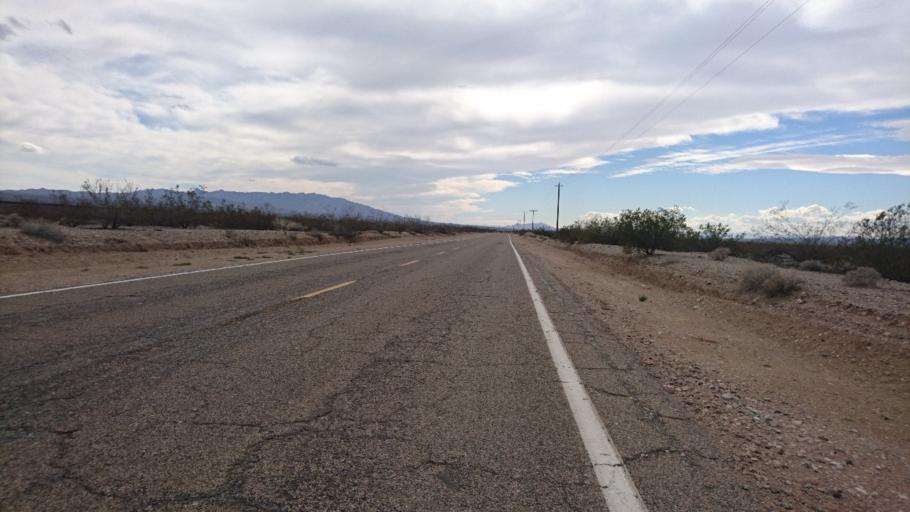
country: US
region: California
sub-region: San Bernardino County
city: Needles
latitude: 34.7795
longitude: -115.2078
